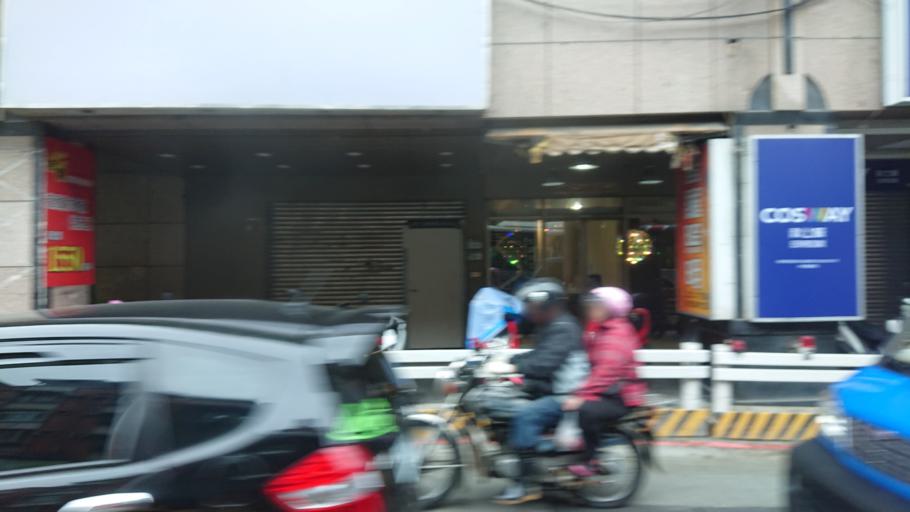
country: TW
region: Taipei
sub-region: Taipei
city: Banqiao
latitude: 24.9947
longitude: 121.4797
